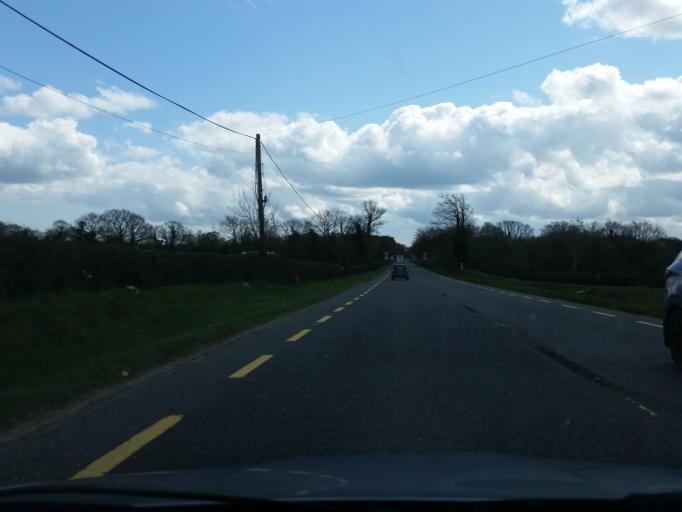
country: IE
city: Kentstown
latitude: 53.6451
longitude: -6.5061
